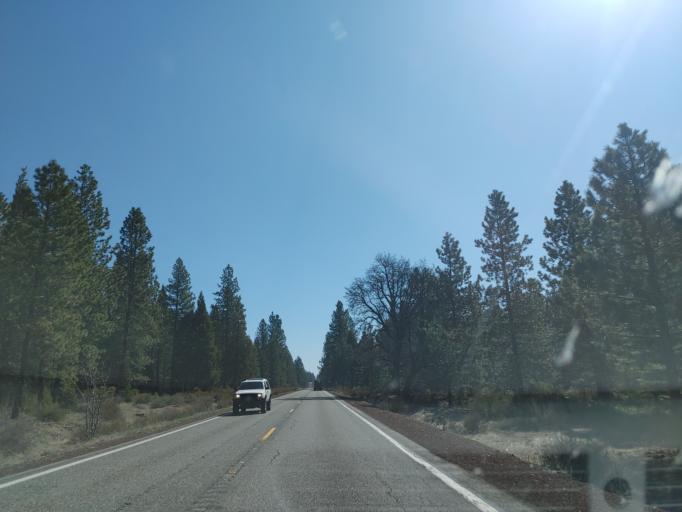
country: US
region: California
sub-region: Siskiyou County
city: McCloud
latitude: 41.2533
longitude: -122.0896
